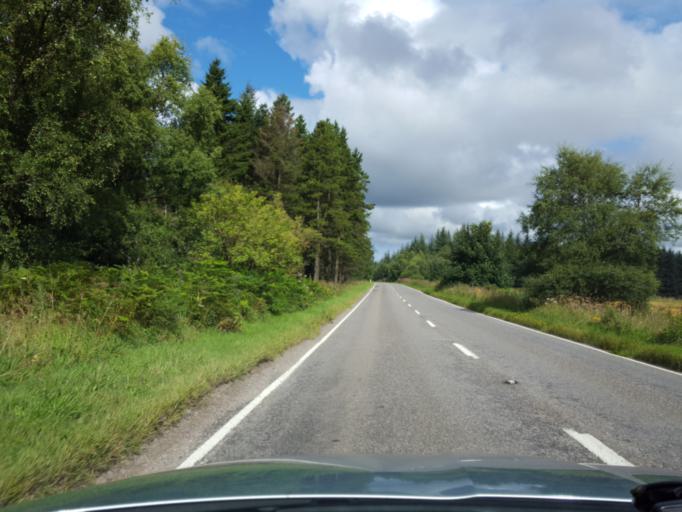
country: GB
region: Scotland
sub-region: Moray
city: Lhanbryd
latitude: 57.5740
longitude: -3.2646
